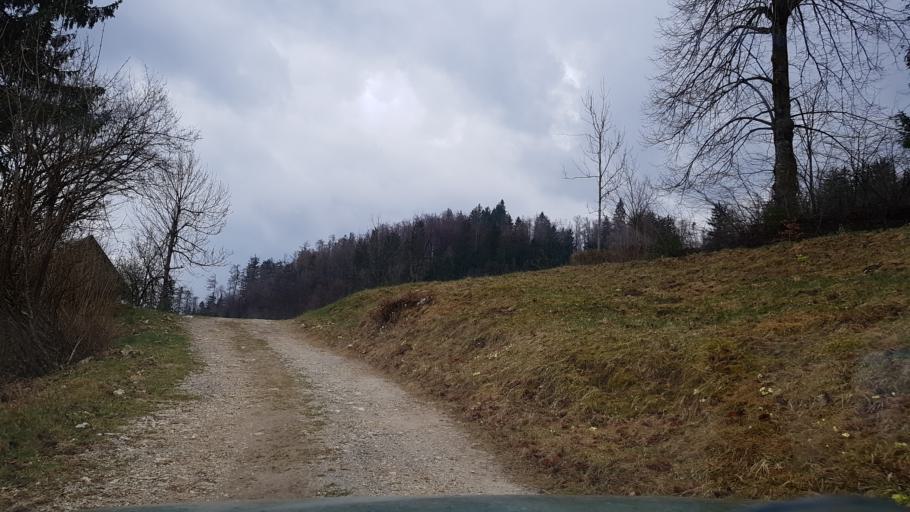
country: SI
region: Cerkno
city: Cerkno
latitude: 46.1383
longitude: 13.8871
